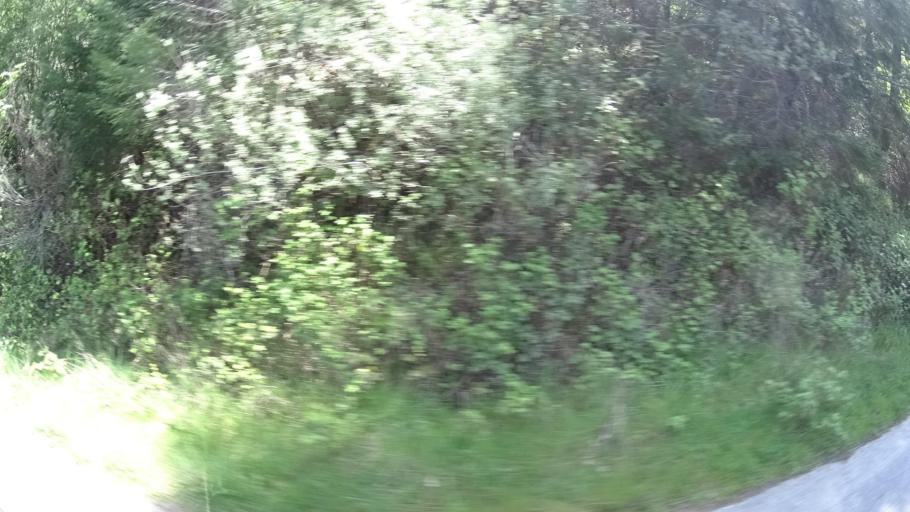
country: US
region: California
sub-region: Humboldt County
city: Redway
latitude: 40.2010
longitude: -123.5190
